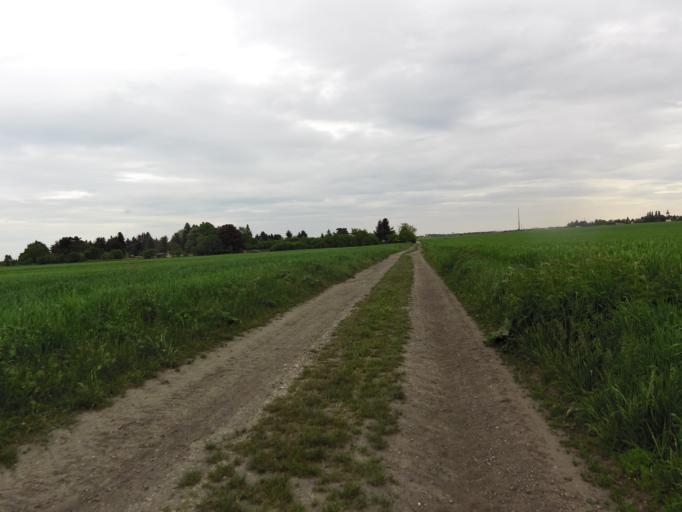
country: DE
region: Saxony
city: Markranstadt
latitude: 51.2827
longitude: 12.2872
